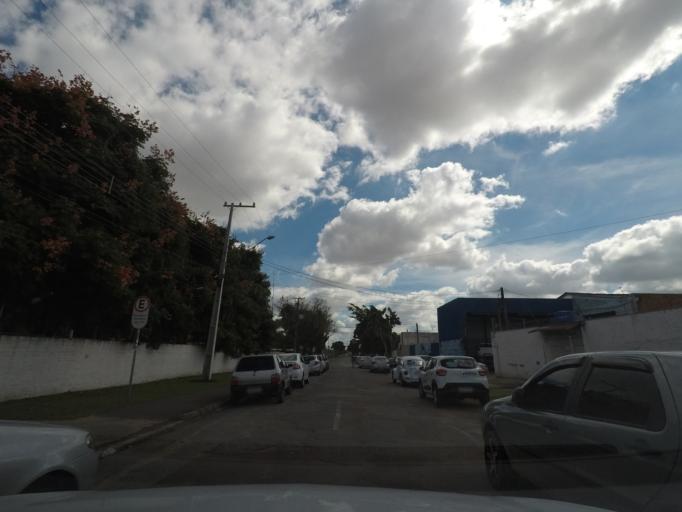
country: BR
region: Parana
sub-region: Sao Jose Dos Pinhais
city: Sao Jose dos Pinhais
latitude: -25.5030
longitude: -49.2271
